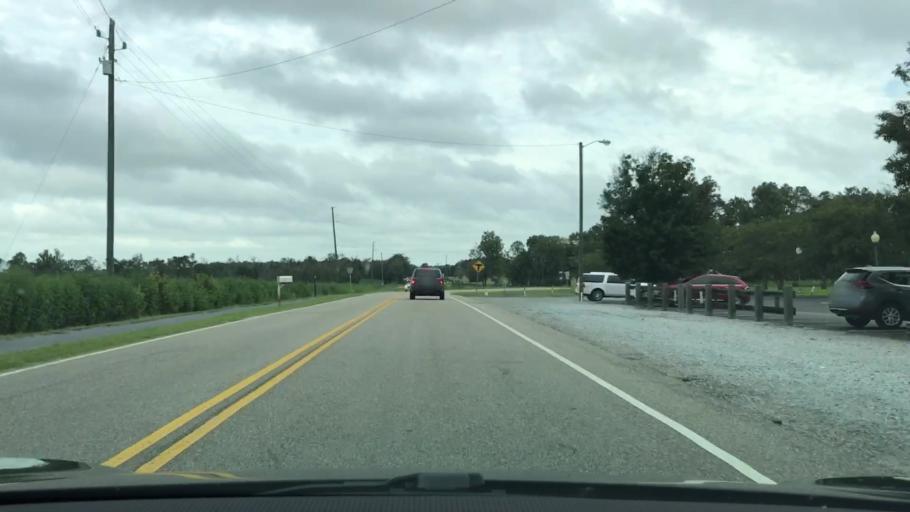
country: US
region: Alabama
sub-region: Montgomery County
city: Pike Road
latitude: 32.3128
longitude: -86.0473
